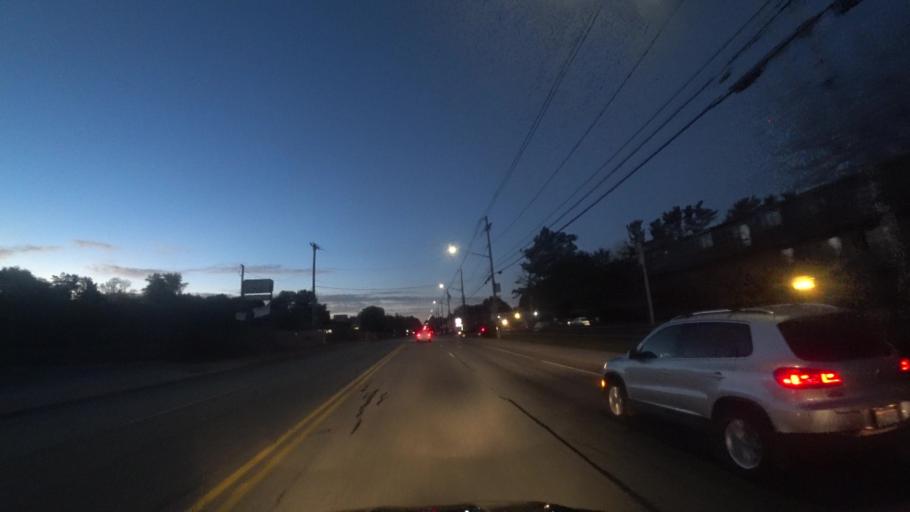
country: US
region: Massachusetts
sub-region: Middlesex County
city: North Reading
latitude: 42.5694
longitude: -71.1091
